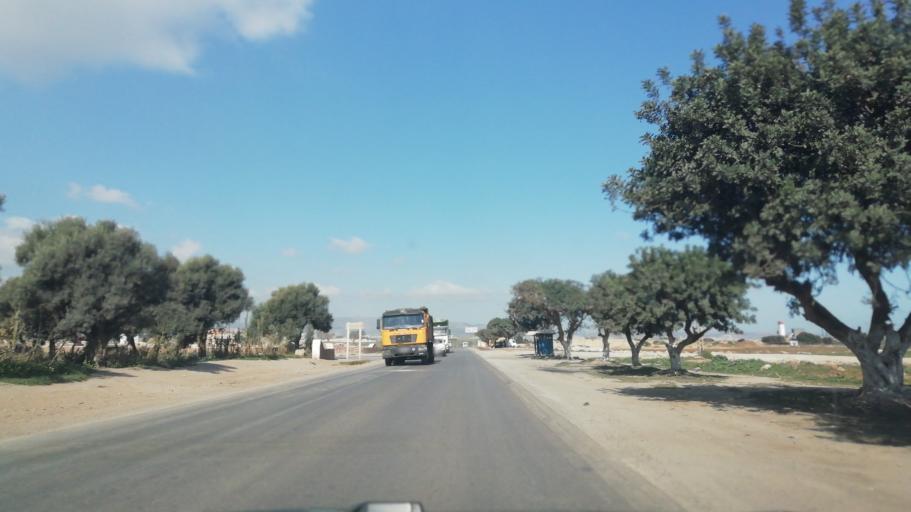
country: DZ
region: Oran
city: Ain el Bya
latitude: 35.7804
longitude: -0.2819
